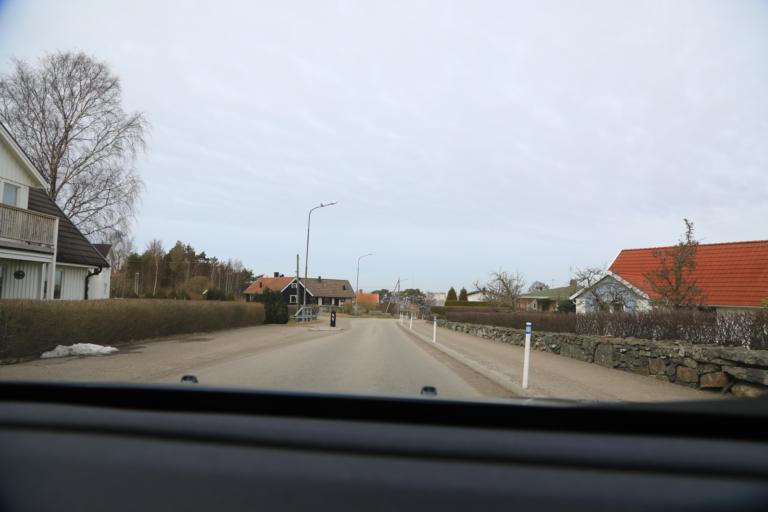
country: SE
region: Halland
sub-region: Kungsbacka Kommun
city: Frillesas
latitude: 57.2345
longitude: 12.1235
